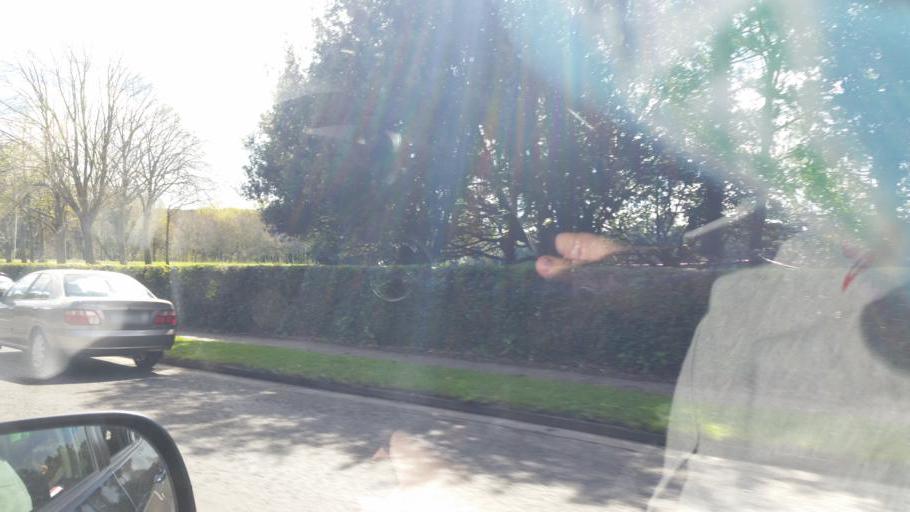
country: IE
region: Leinster
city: Dollymount
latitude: 53.3758
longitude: -6.1681
